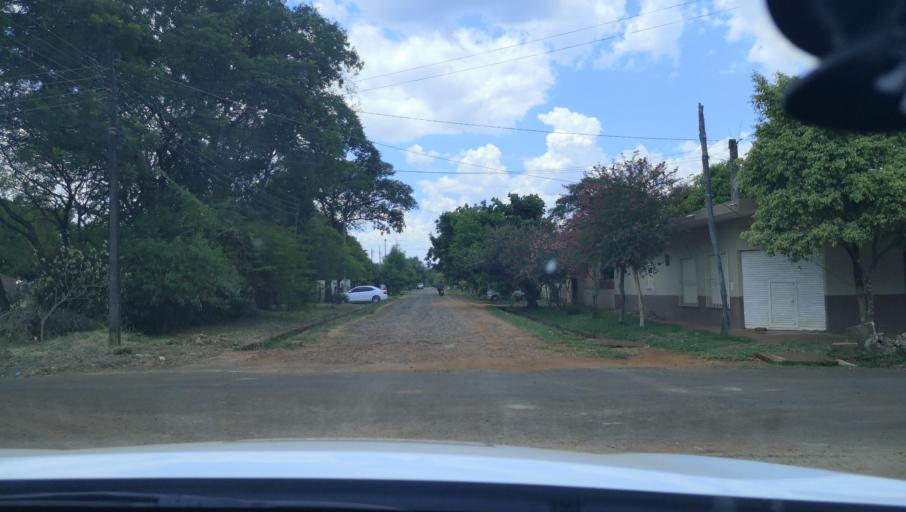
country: PY
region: Itapua
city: Carmen del Parana
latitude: -27.1685
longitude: -56.2359
